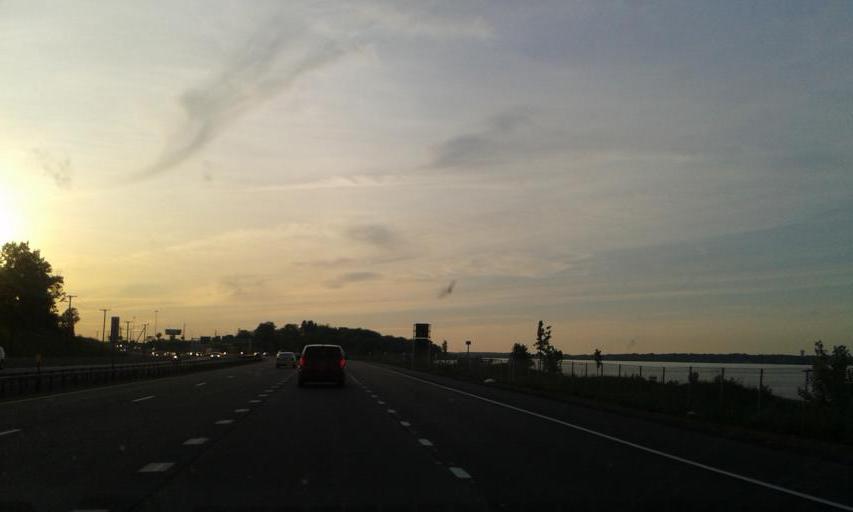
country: US
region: New York
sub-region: Onondaga County
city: Solvay
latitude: 43.0680
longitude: -76.2000
